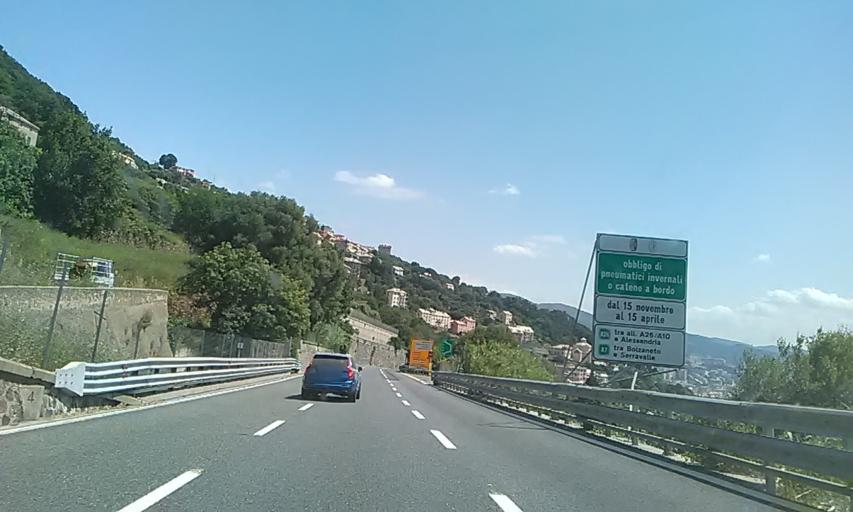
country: IT
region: Liguria
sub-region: Provincia di Genova
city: Mele
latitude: 44.4198
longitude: 8.7264
